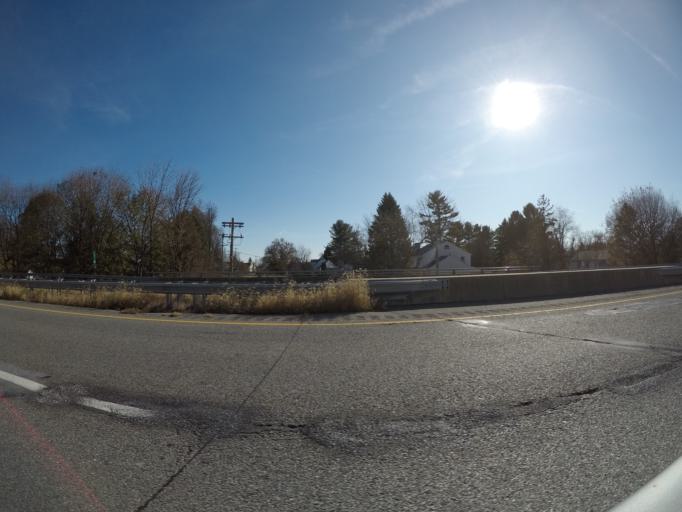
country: US
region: Pennsylvania
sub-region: Chester County
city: Parkesburg
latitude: 39.9859
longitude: -75.8929
